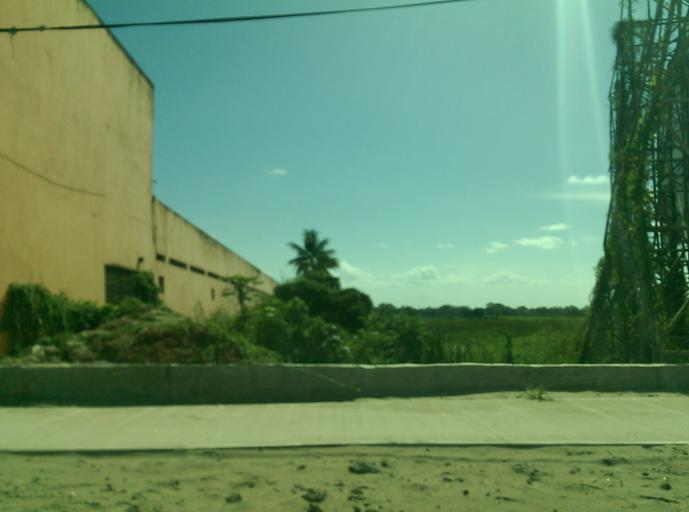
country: MX
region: Tabasco
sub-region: Centro
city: Anacleto Canabal 2da. Seccion
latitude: 17.9851
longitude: -92.9979
